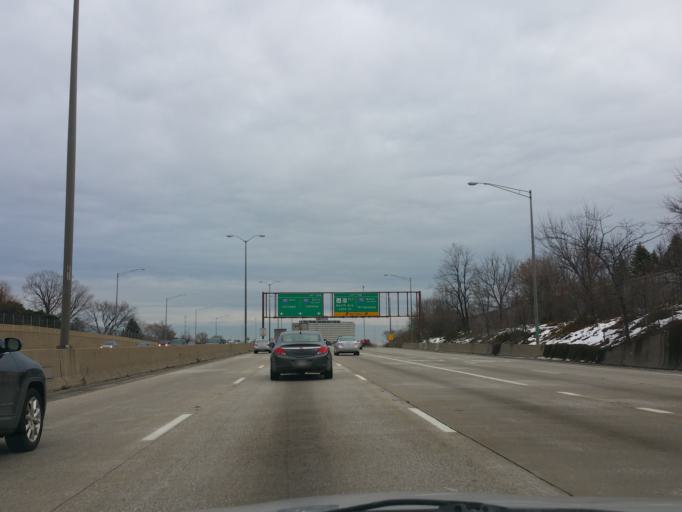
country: US
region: Illinois
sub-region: DuPage County
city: Elmhurst
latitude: 41.9094
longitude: -87.9302
